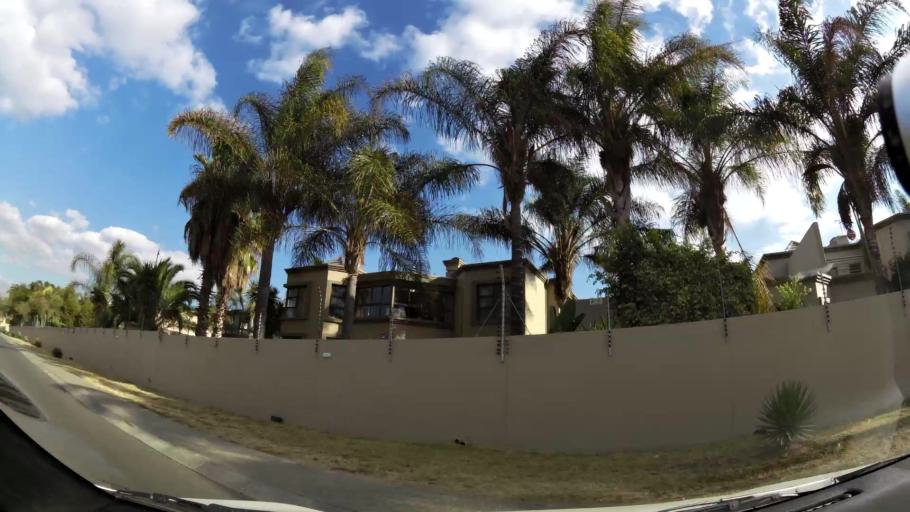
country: ZA
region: Gauteng
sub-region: City of Johannesburg Metropolitan Municipality
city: Diepsloot
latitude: -26.0009
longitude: 28.0172
